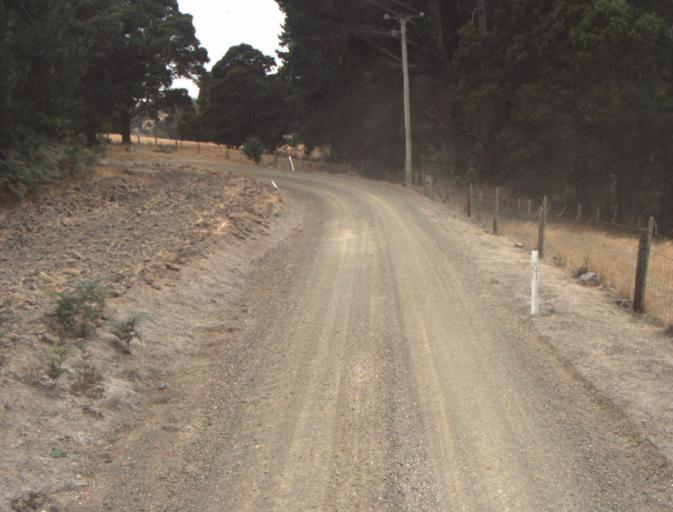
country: AU
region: Tasmania
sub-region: Dorset
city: Bridport
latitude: -41.1594
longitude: 147.2121
